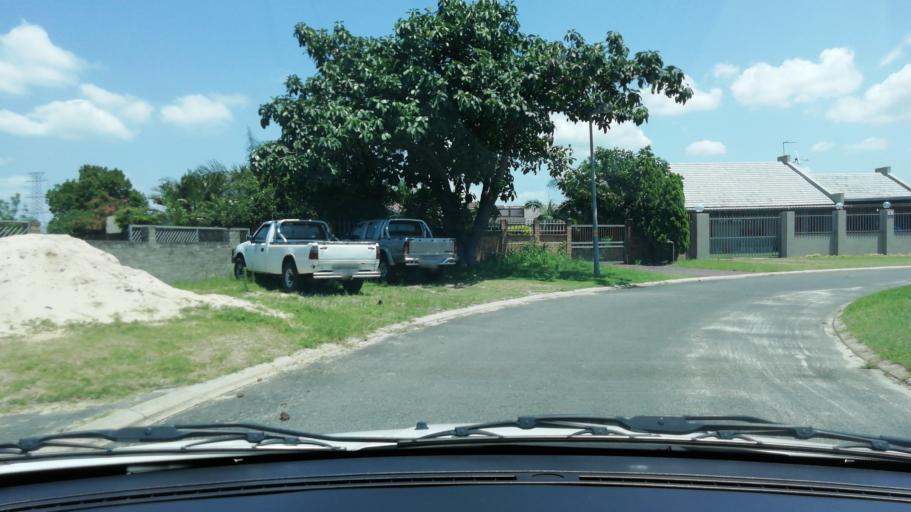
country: ZA
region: KwaZulu-Natal
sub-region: uThungulu District Municipality
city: Richards Bay
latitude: -28.7370
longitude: 32.0462
